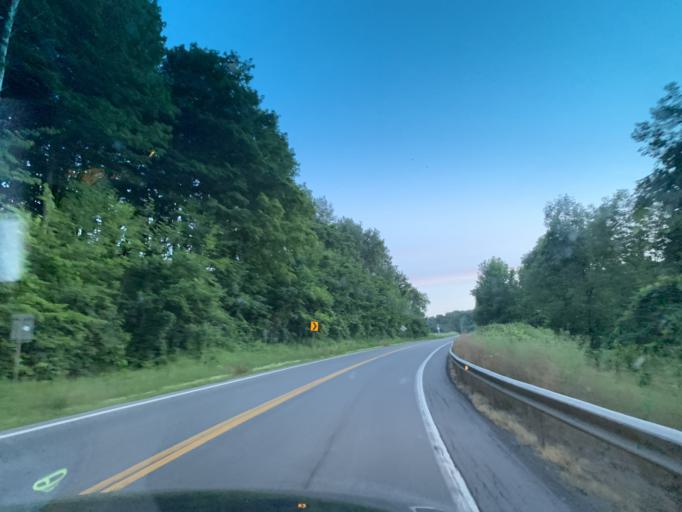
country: US
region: New York
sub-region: Chenango County
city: New Berlin
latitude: 42.7146
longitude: -75.3127
